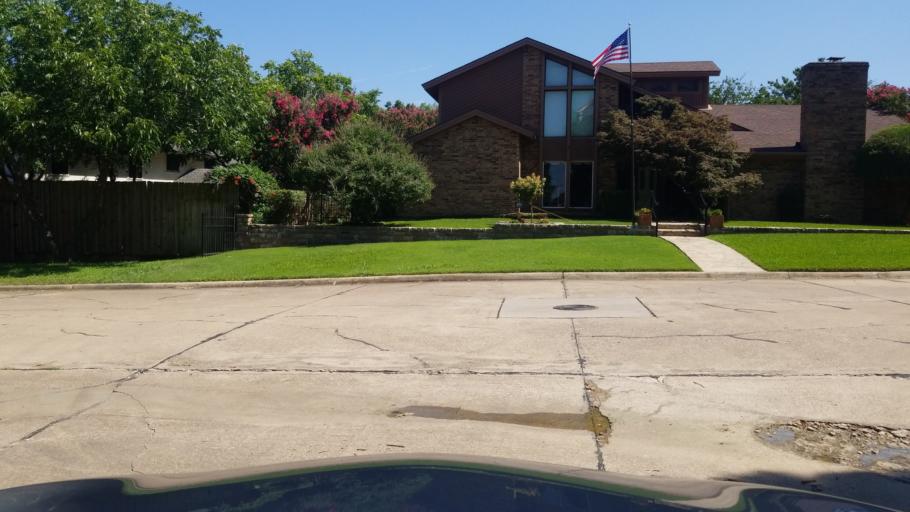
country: US
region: Texas
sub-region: Dallas County
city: Grand Prairie
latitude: 32.6844
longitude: -96.9969
